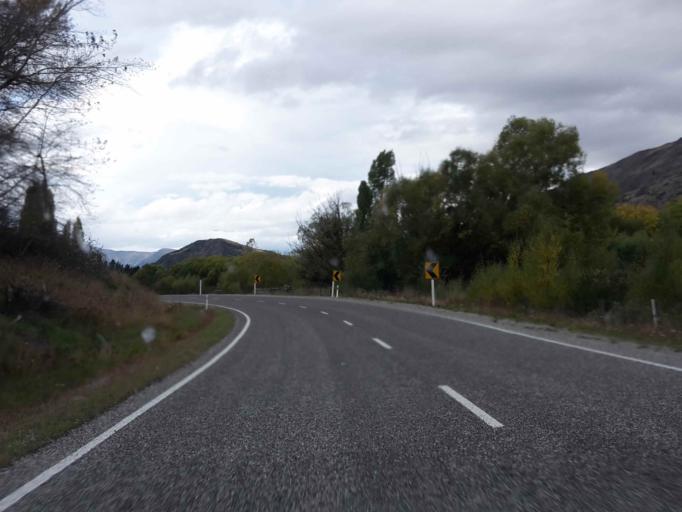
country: NZ
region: Otago
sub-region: Queenstown-Lakes District
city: Wanaka
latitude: -44.7464
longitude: 169.1264
